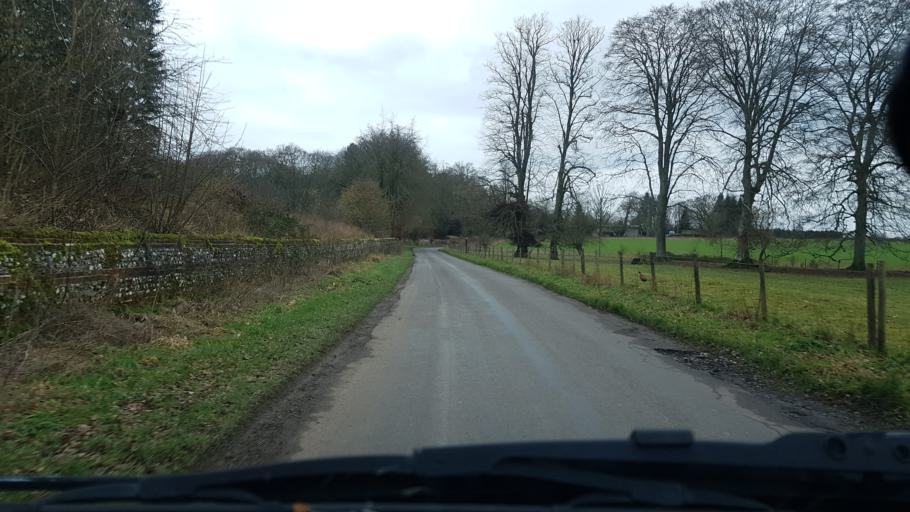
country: GB
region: England
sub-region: Wiltshire
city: Shalbourne
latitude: 51.3262
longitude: -1.5544
